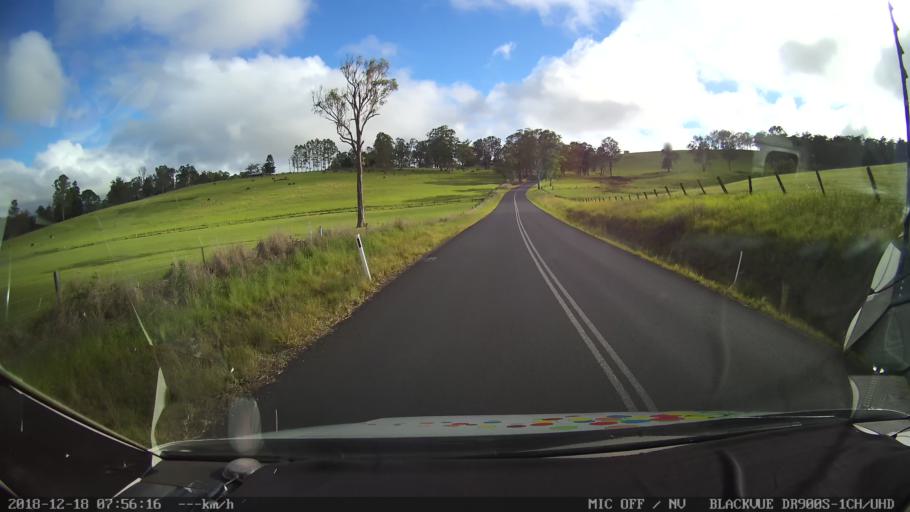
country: AU
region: New South Wales
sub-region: Kyogle
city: Kyogle
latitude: -28.4004
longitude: 152.6049
